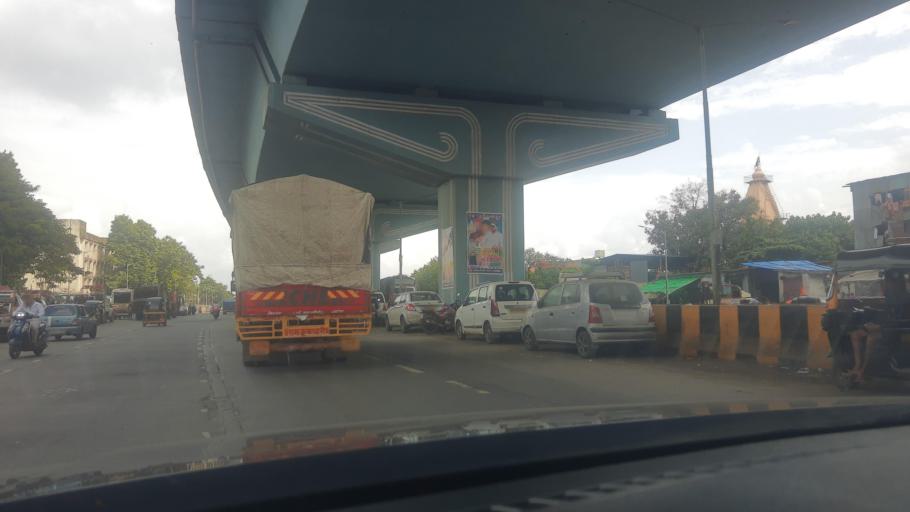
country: IN
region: Maharashtra
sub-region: Mumbai Suburban
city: Mumbai
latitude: 19.0611
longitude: 72.9202
